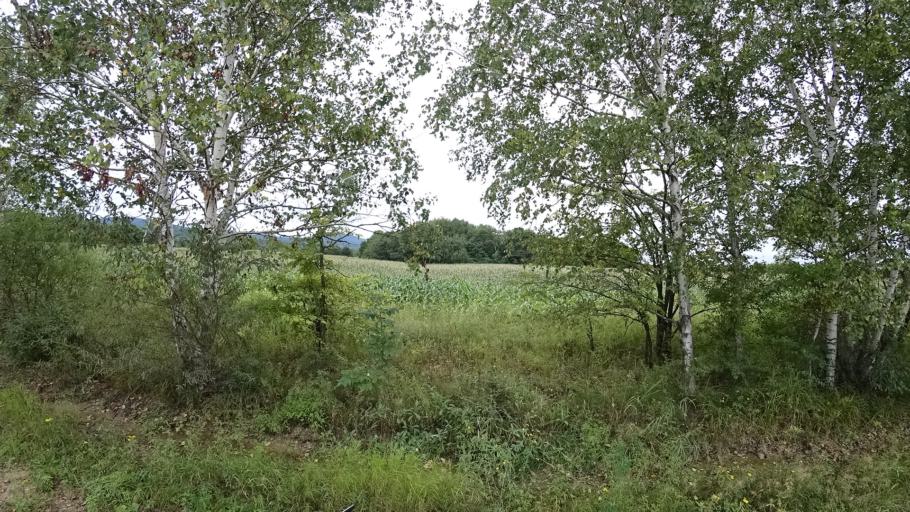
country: RU
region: Primorskiy
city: Rettikhovka
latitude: 44.1596
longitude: 132.6943
